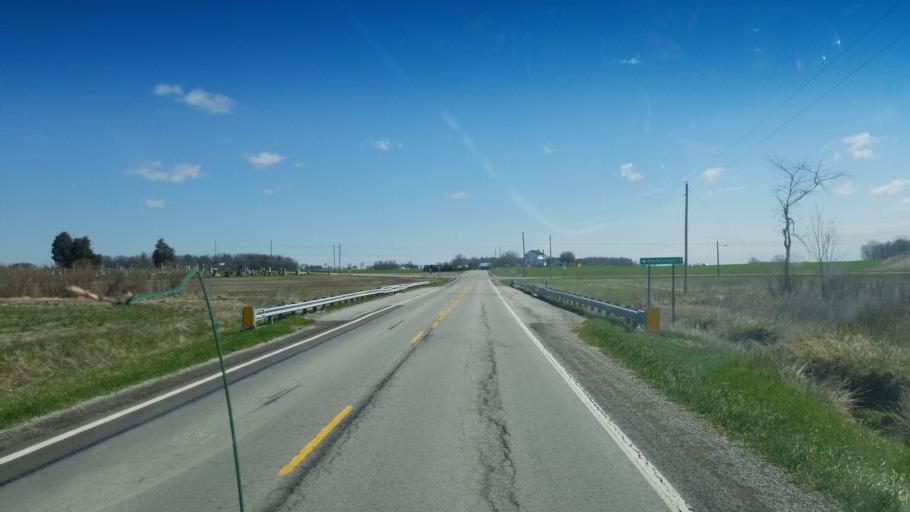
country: US
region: Ohio
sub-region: Crawford County
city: Bucyrus
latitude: 40.8839
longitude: -82.8560
